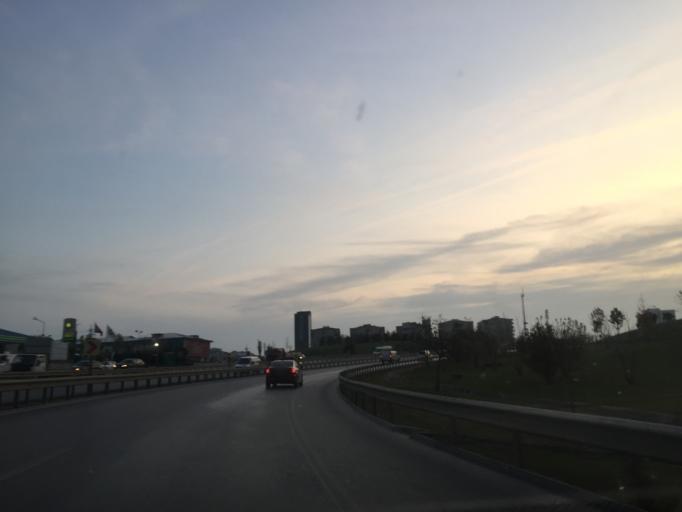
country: TR
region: Istanbul
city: Samandira
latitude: 40.9707
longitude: 29.2199
